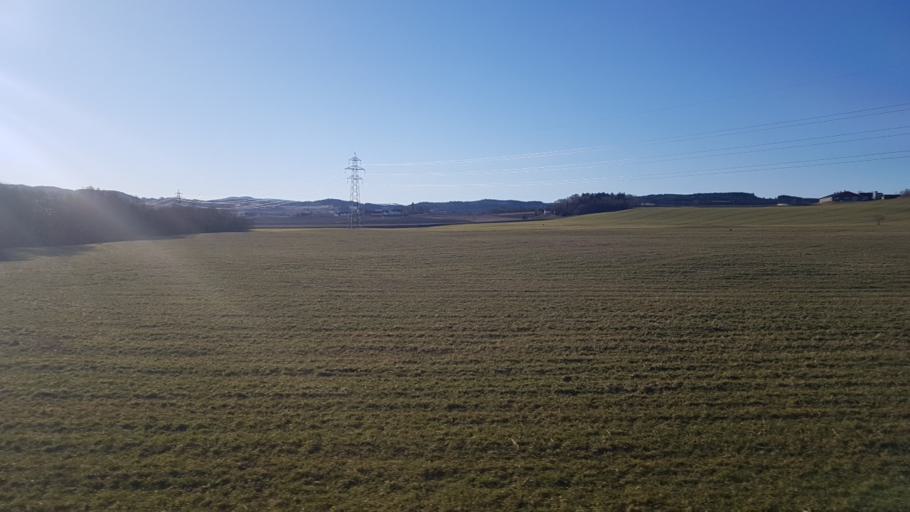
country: NO
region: Nord-Trondelag
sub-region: Levanger
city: Skogn
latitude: 63.6950
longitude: 11.1803
